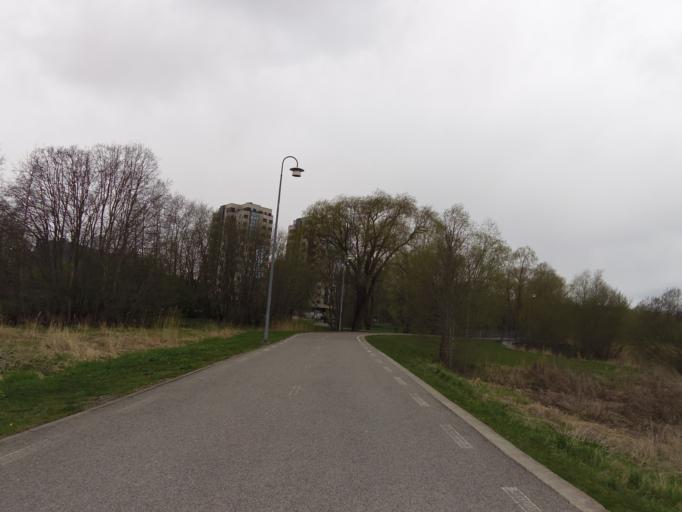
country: EE
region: Harju
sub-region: Saue vald
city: Laagri
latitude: 59.4289
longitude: 24.6577
